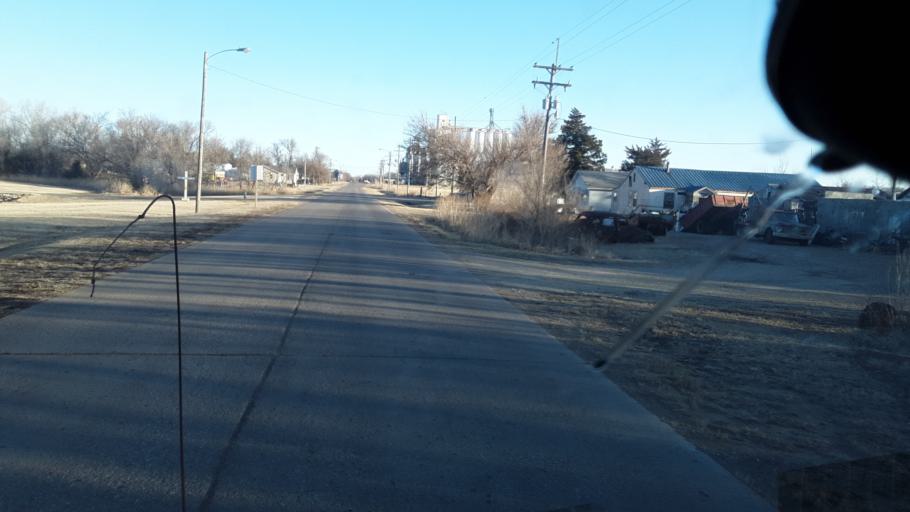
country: US
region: Kansas
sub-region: Rice County
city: Lyons
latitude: 38.3483
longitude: -98.3495
